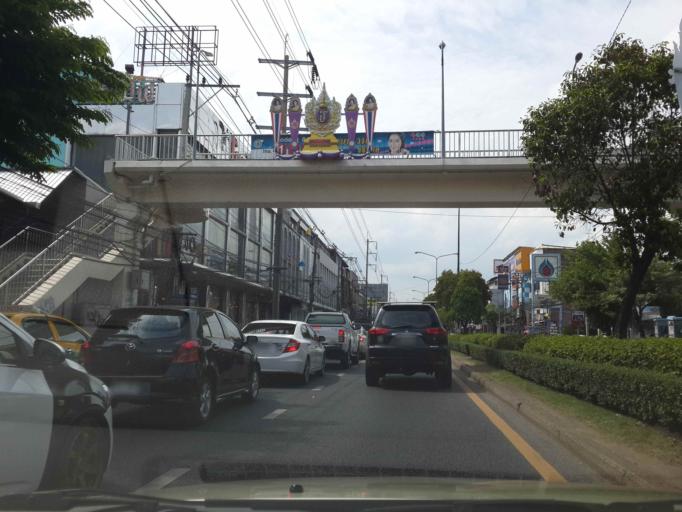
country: TH
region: Bangkok
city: Bang Kapi
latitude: 13.7577
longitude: 100.6458
